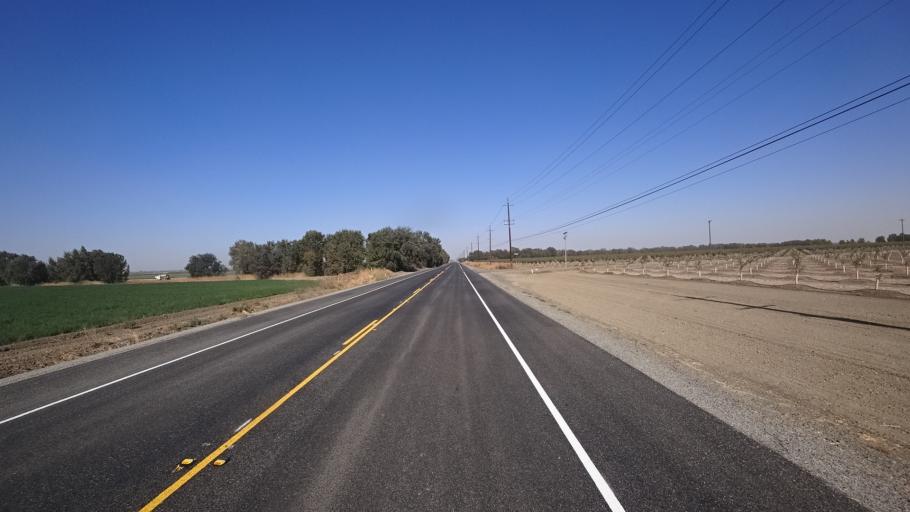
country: US
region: California
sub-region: Yolo County
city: Woodland
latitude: 38.6254
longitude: -121.7296
